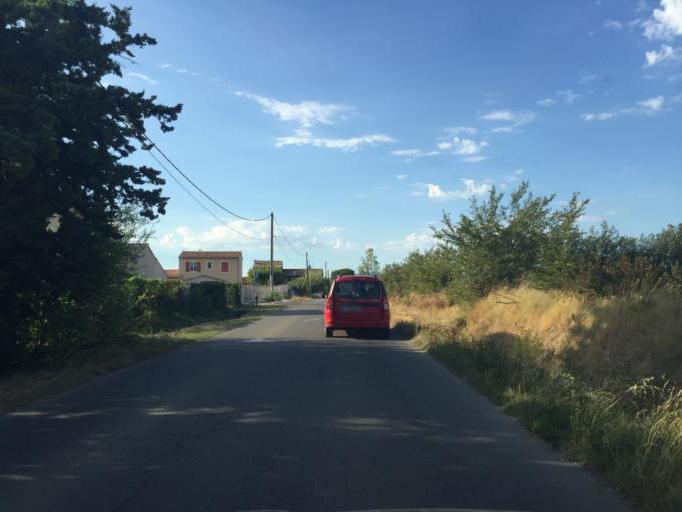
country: FR
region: Provence-Alpes-Cote d'Azur
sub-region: Departement du Vaucluse
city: Pernes-les-Fontaines
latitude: 44.0082
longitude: 5.0555
